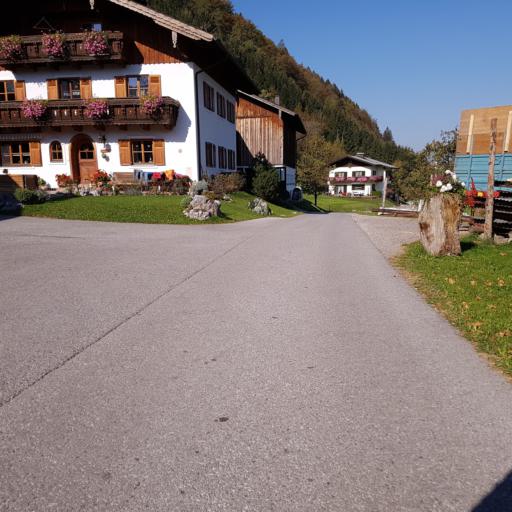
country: AT
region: Salzburg
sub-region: Politischer Bezirk Hallein
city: Hallein
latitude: 47.6651
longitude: 13.1109
